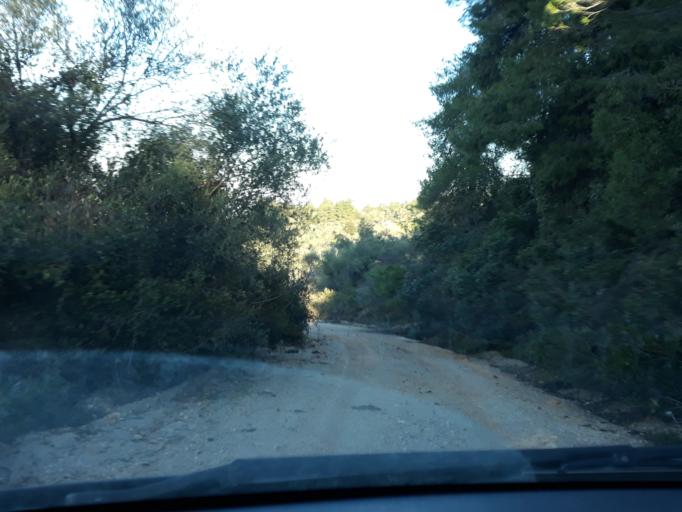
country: GR
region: Central Greece
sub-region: Nomos Voiotias
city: Asopia
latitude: 38.2708
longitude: 23.5320
